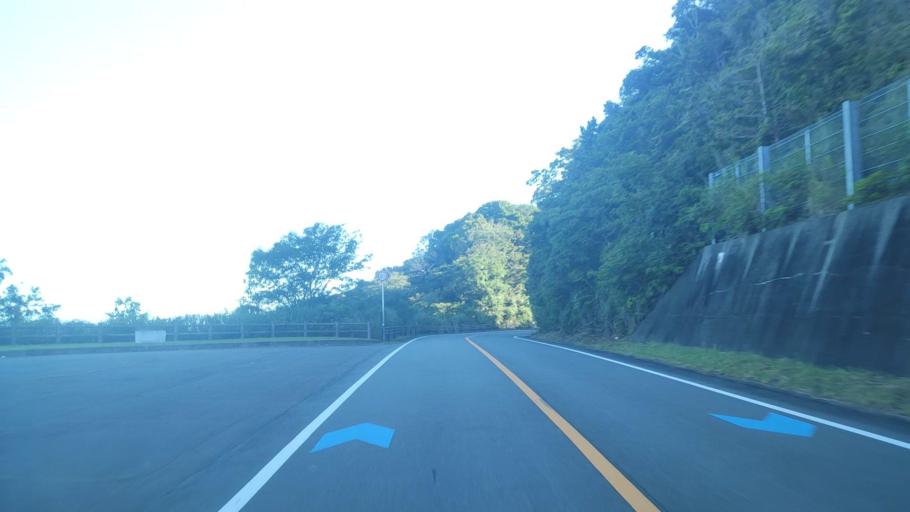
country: JP
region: Mie
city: Toba
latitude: 34.4104
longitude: 136.9008
